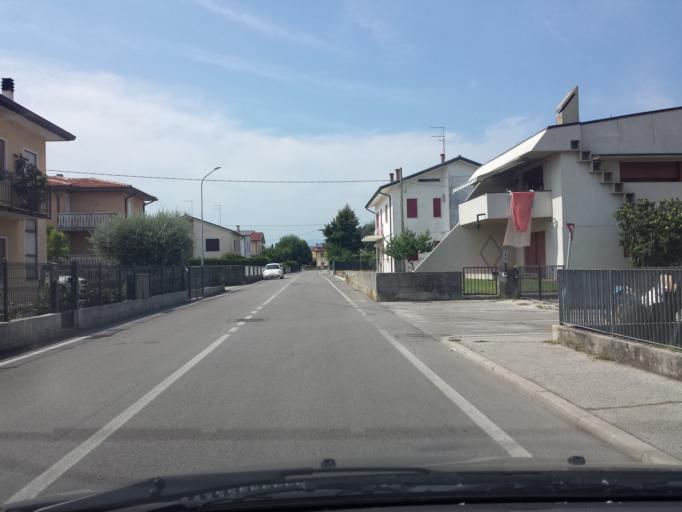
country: IT
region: Veneto
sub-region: Provincia di Vicenza
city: Sandrigo
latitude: 45.6604
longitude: 11.5919
